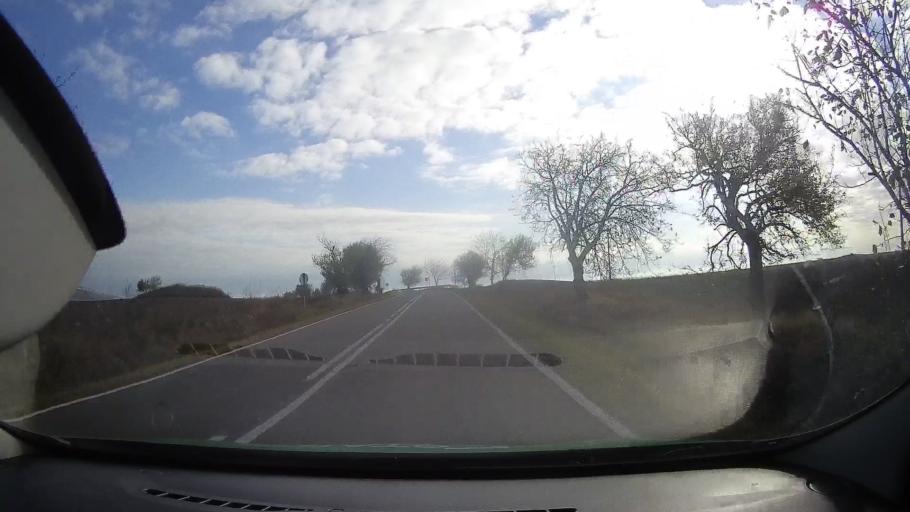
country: RO
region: Tulcea
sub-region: Comuna Bestepe
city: Bestepe
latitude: 45.0783
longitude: 29.0425
